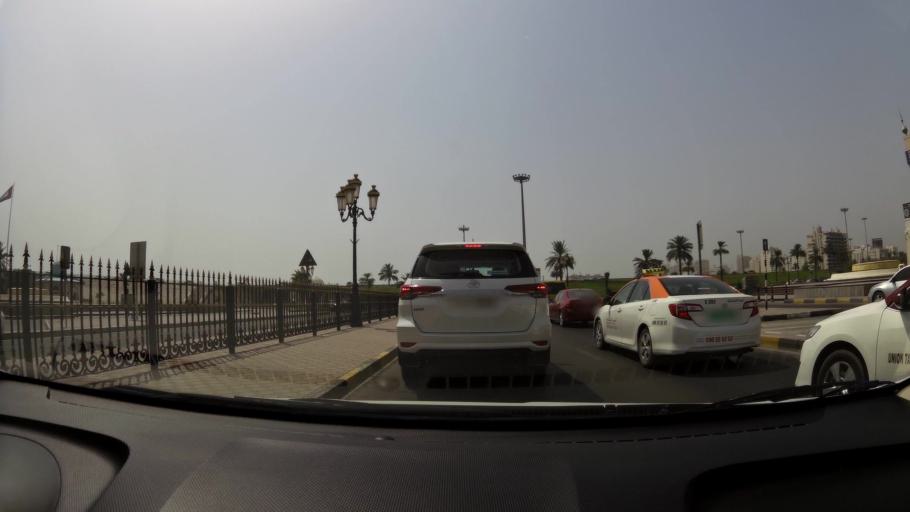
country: AE
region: Ash Shariqah
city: Sharjah
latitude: 25.3479
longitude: 55.3834
